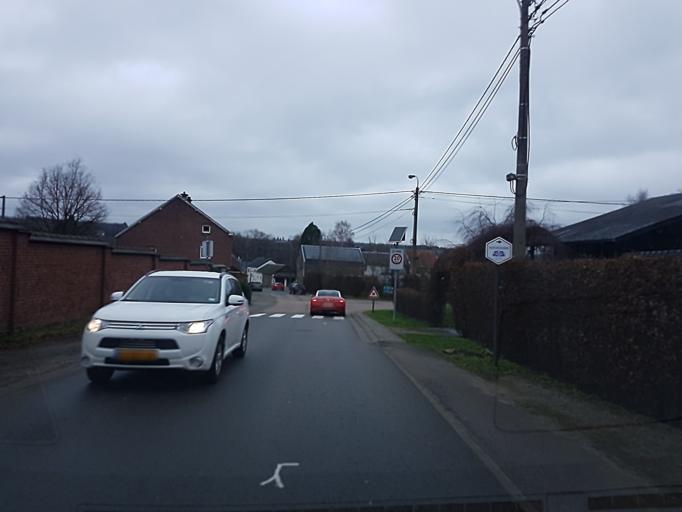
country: BE
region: Wallonia
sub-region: Province de Liege
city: Spa
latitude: 50.4944
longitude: 5.8952
